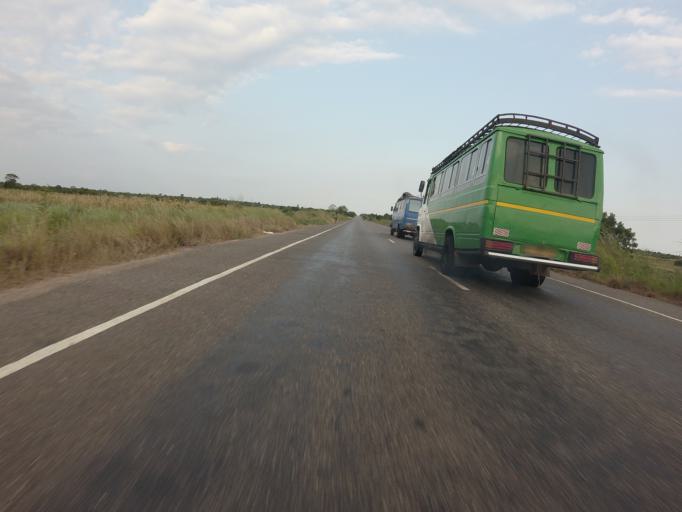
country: GH
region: Volta
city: Anloga
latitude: 6.0893
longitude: 0.5347
